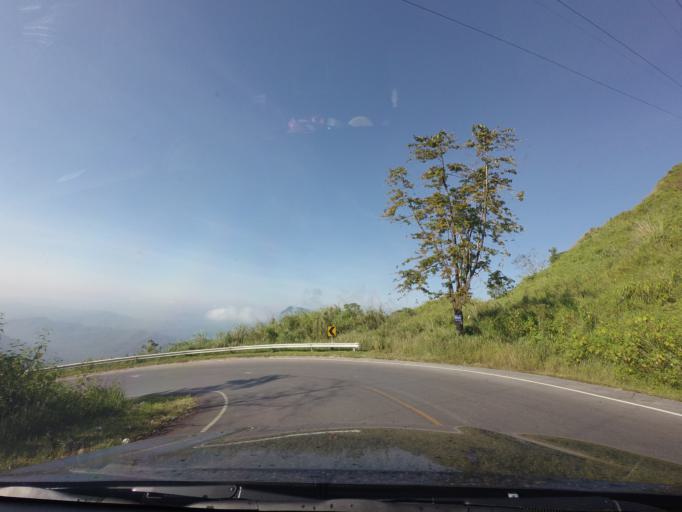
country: TH
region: Phetchabun
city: Lom Kao
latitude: 16.8791
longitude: 101.1024
